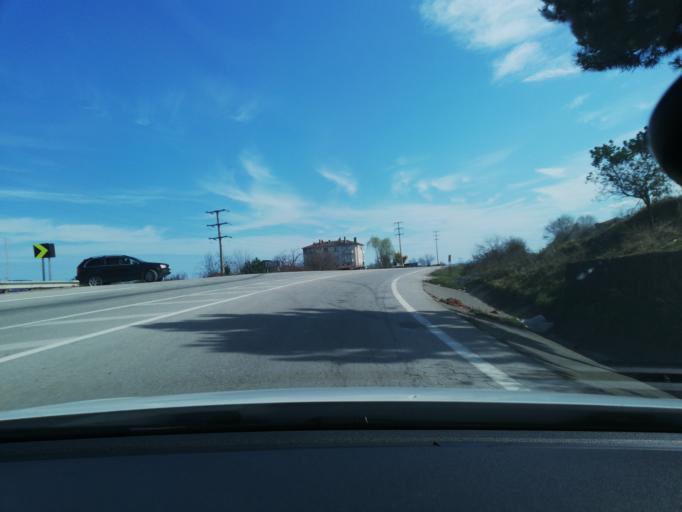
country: TR
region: Duzce
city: Akcakoca
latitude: 41.0832
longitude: 31.1321
